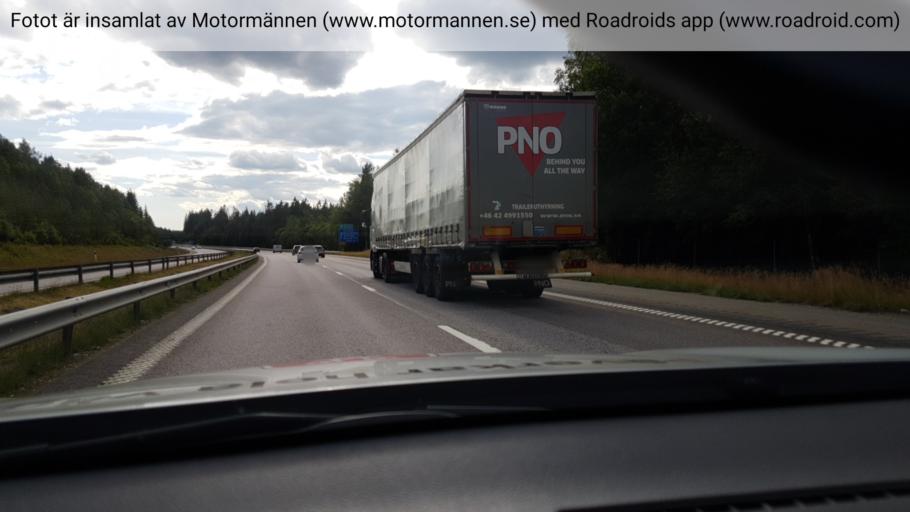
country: SE
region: Vaestra Goetaland
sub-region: Bollebygds Kommun
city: Bollebygd
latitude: 57.6700
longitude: 12.6185
